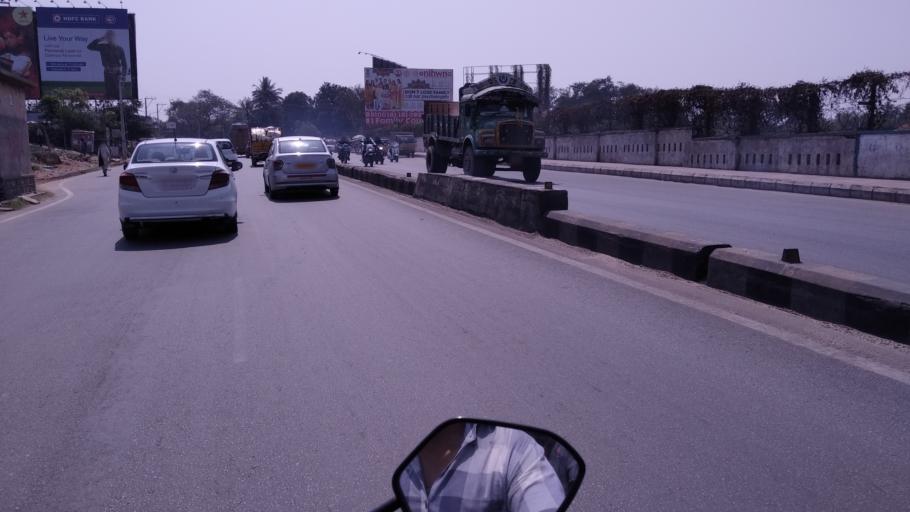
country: IN
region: Telangana
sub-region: Hyderabad
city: Malkajgiri
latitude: 17.4530
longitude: 78.4860
